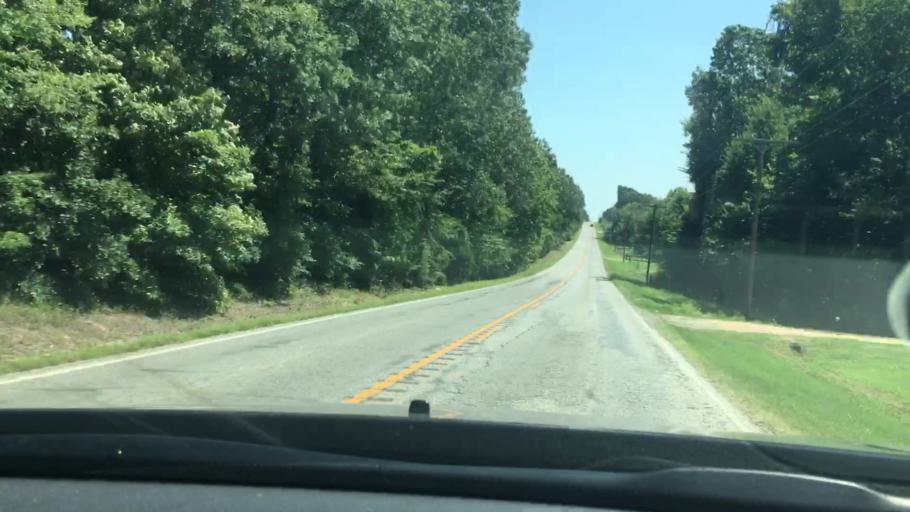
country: US
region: Oklahoma
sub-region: Johnston County
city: Tishomingo
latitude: 34.2377
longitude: -96.5942
